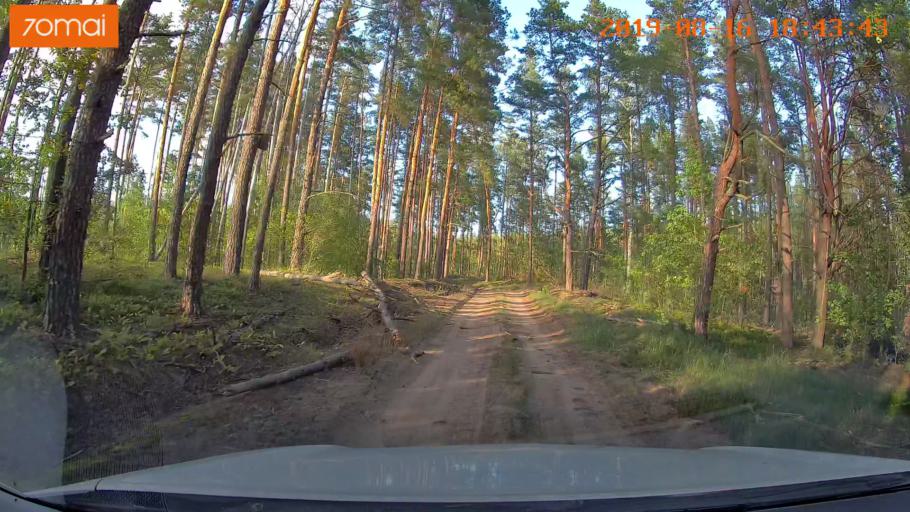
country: BY
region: Mogilev
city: Asipovichy
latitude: 53.2185
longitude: 28.6546
